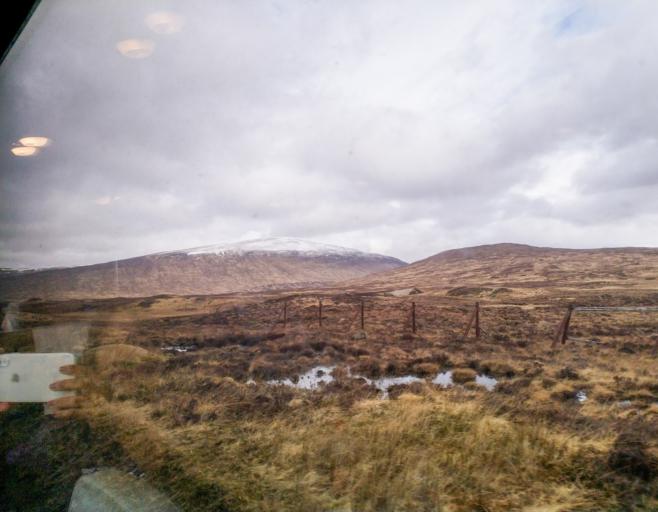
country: GB
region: Scotland
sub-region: Highland
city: Spean Bridge
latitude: 56.7432
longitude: -4.6683
